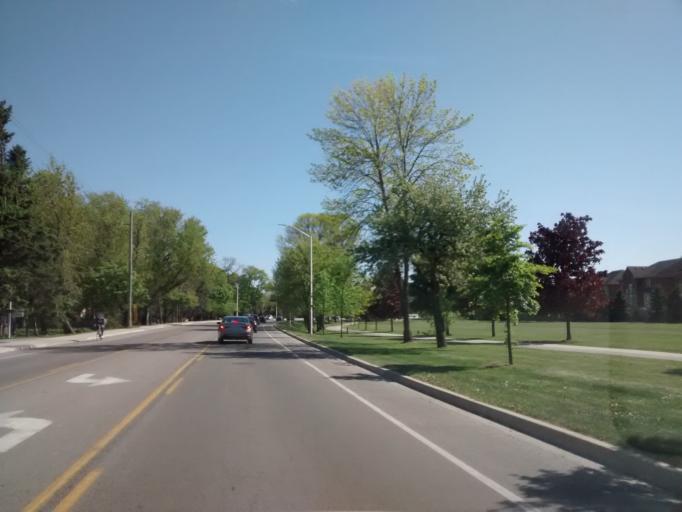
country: CA
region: Ontario
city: Oakville
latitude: 43.3794
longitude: -79.7175
